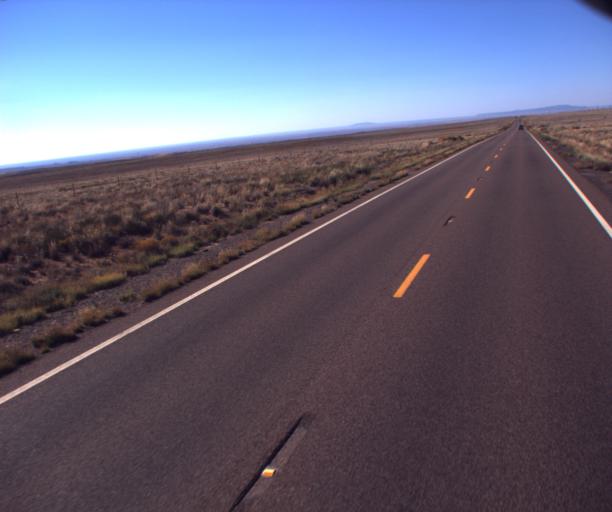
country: US
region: Arizona
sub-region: Navajo County
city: Winslow
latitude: 35.0959
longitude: -110.5402
